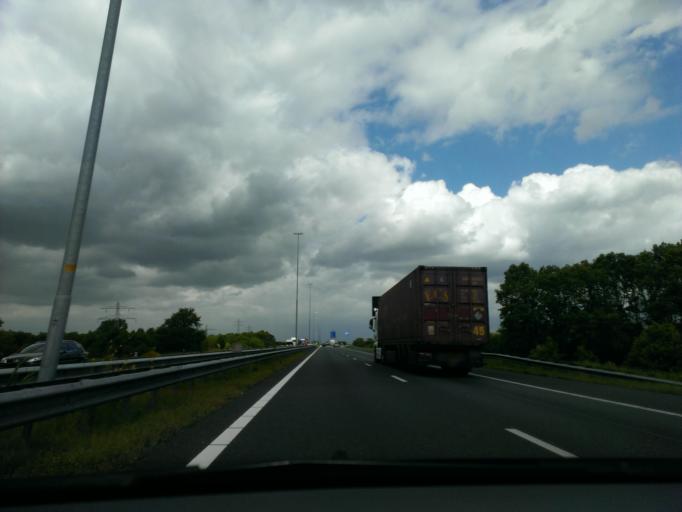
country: NL
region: North Brabant
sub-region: Gemeente Cuijk
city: Cuijk
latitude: 51.7489
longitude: 5.8407
